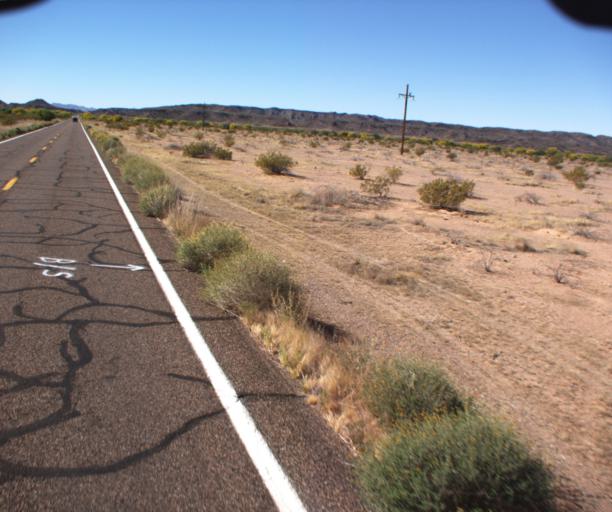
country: US
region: Arizona
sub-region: Pima County
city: Ajo
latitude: 32.5880
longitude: -112.8725
